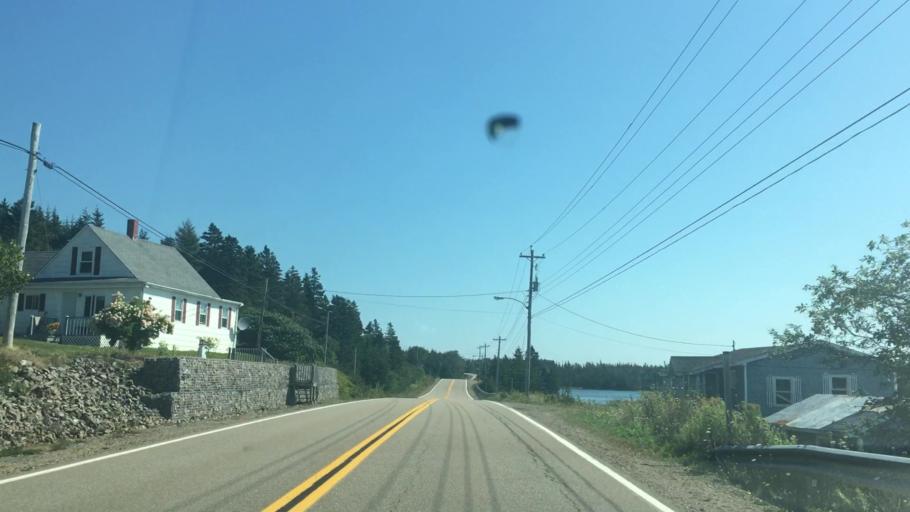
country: CA
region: Nova Scotia
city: Antigonish
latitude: 45.0225
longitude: -62.0158
